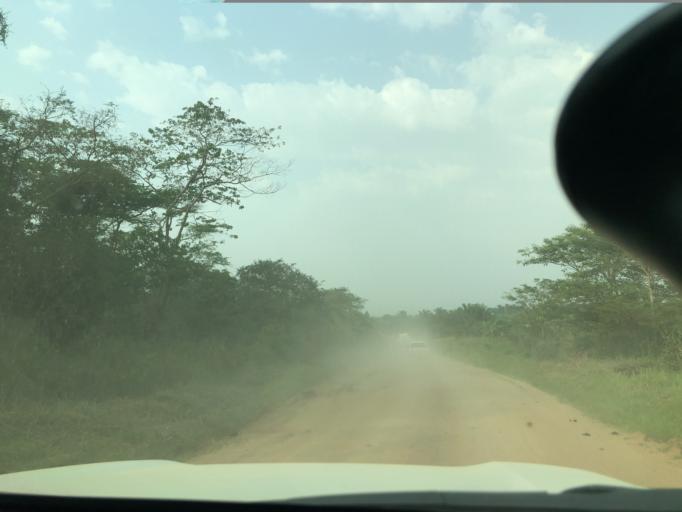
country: UG
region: Western Region
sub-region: Kasese District
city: Margherita
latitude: 0.2064
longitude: 29.6749
